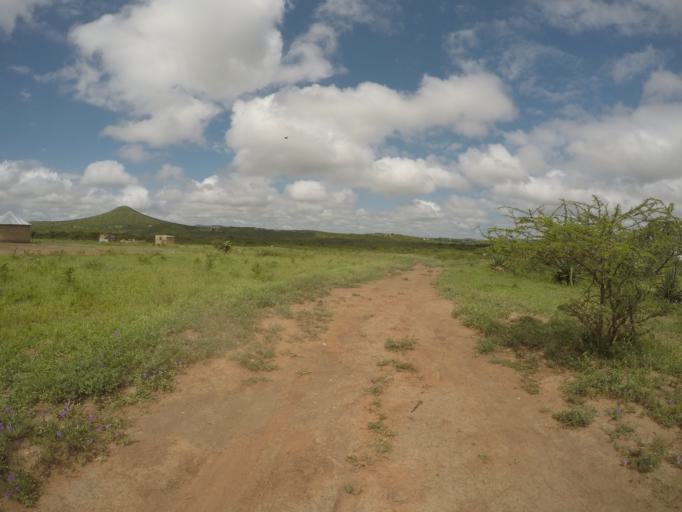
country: ZA
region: KwaZulu-Natal
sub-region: uThungulu District Municipality
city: Empangeni
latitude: -28.5845
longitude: 31.8526
